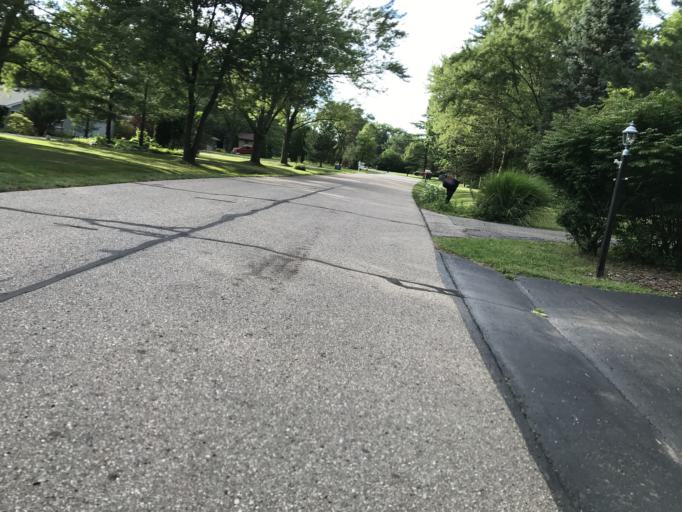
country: US
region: Michigan
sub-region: Oakland County
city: Farmington Hills
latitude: 42.4799
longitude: -83.3456
